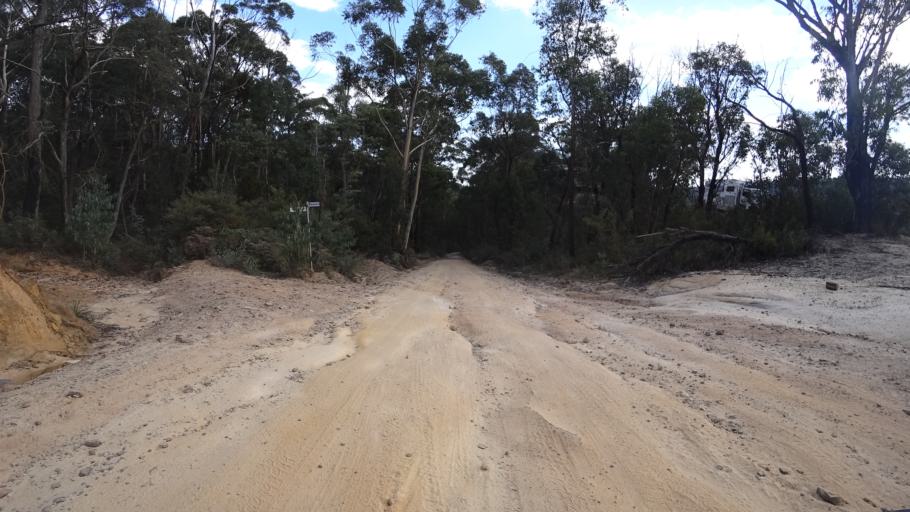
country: AU
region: New South Wales
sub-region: Lithgow
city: Lithgow
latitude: -33.4441
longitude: 150.1803
